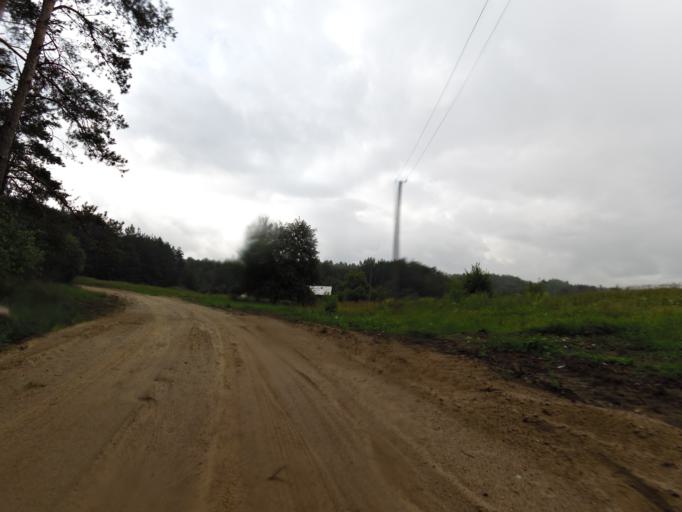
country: LT
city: Grigiskes
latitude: 54.7127
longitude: 25.1119
